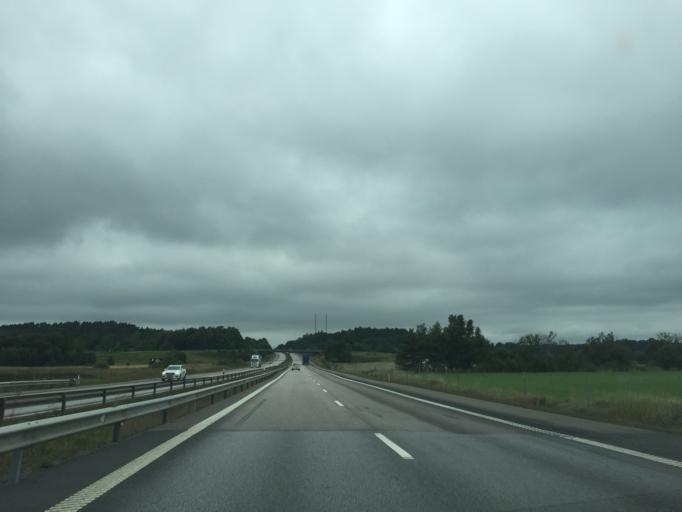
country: SE
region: Halland
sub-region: Kungsbacka Kommun
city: Fjaeras kyrkby
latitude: 57.4159
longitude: 12.1697
